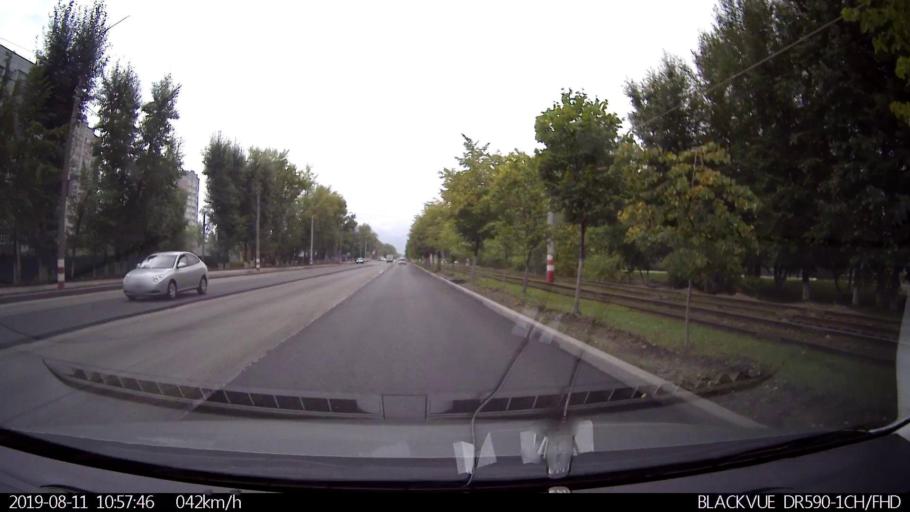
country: RU
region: Ulyanovsk
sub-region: Ulyanovskiy Rayon
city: Ulyanovsk
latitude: 54.2567
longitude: 48.3205
